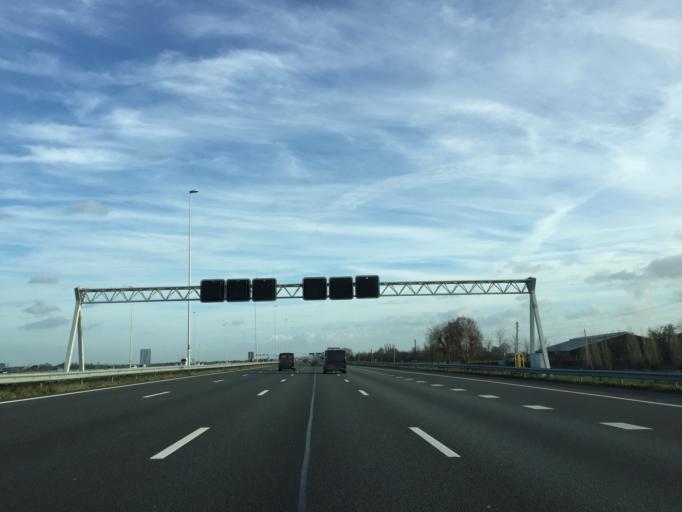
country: NL
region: South Holland
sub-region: Bodegraven-Reeuwijk
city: Bodegraven
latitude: 52.0665
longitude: 4.7632
